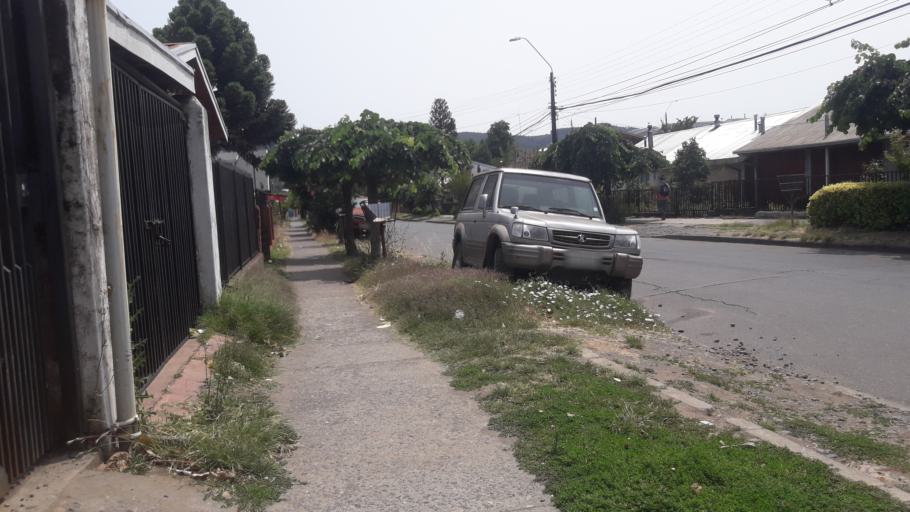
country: CL
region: Biobio
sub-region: Provincia de Biobio
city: Nacimiento
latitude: -37.5045
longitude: -72.6802
